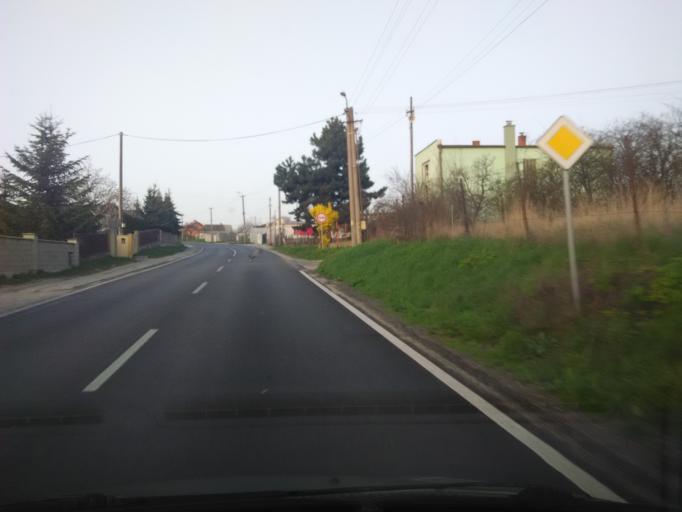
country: SK
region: Nitriansky
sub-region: Okres Nitra
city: Nitra
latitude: 48.2442
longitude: 18.0182
